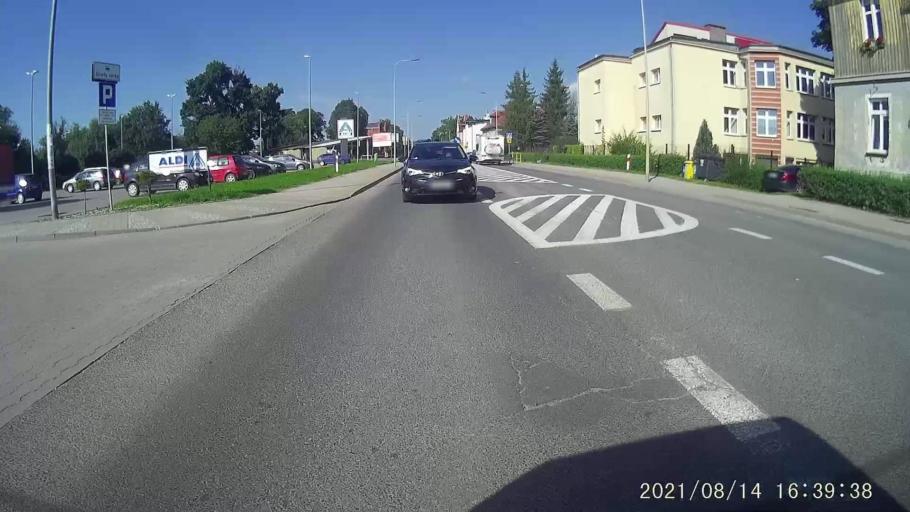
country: PL
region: Lower Silesian Voivodeship
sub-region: Powiat kamiennogorski
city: Kamienna Gora
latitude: 50.7837
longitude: 16.0219
